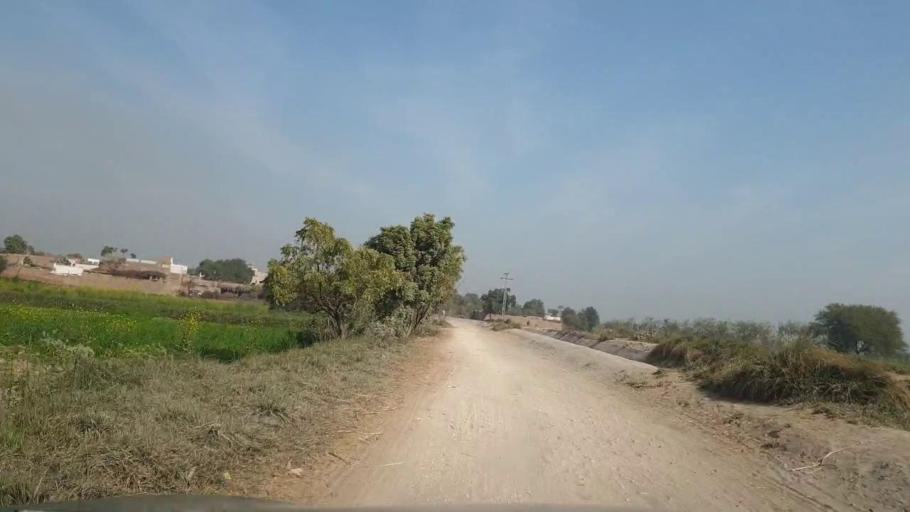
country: PK
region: Sindh
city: Tando Allahyar
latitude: 25.5987
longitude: 68.7221
